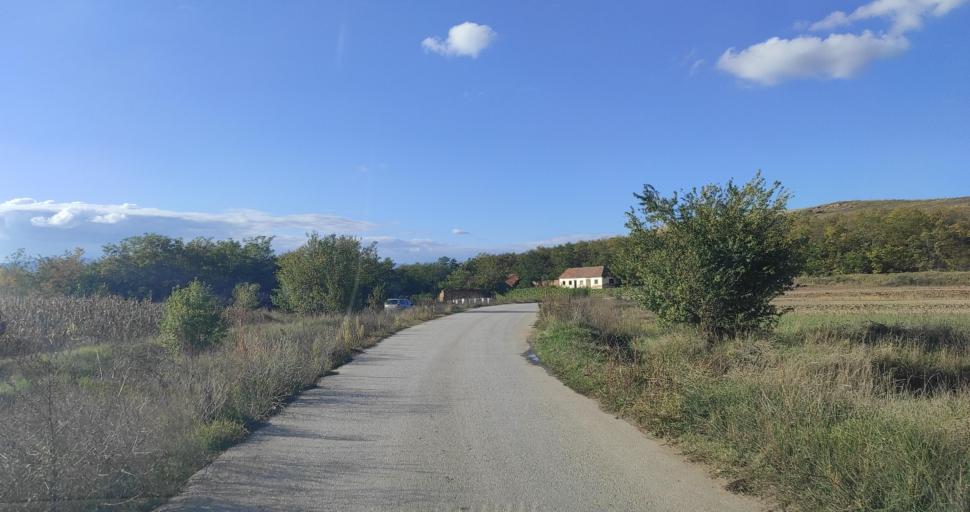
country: MK
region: Prilep
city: Topolcani
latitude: 41.2836
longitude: 21.4208
